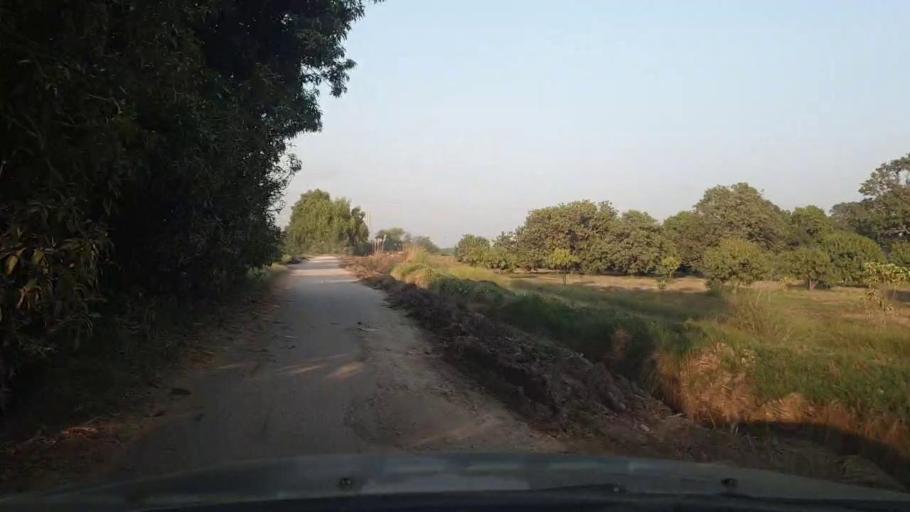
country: PK
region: Sindh
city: Tando Jam
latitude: 25.4256
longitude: 68.4956
